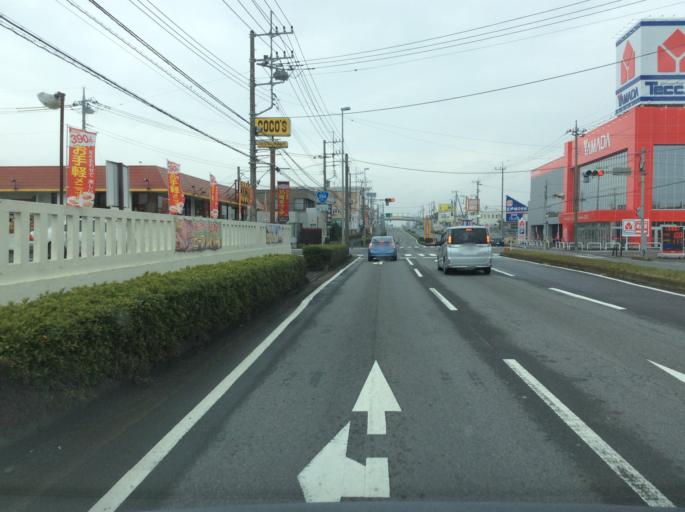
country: JP
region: Ibaraki
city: Mitsukaido
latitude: 35.9771
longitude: 139.9827
